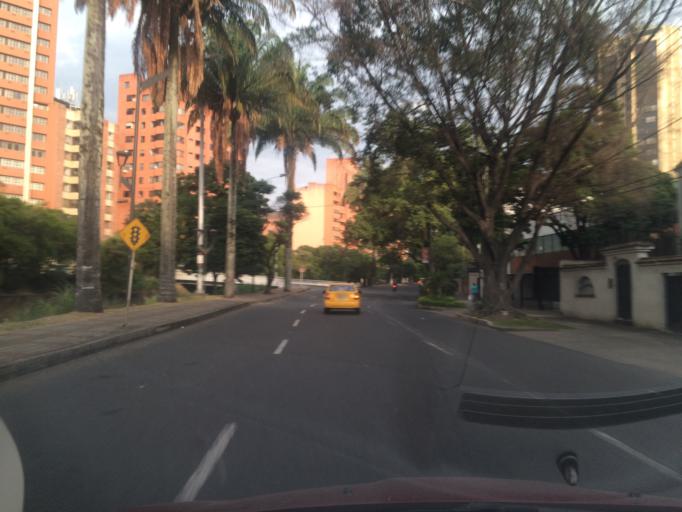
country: CO
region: Valle del Cauca
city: Cali
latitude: 3.4509
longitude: -76.5394
